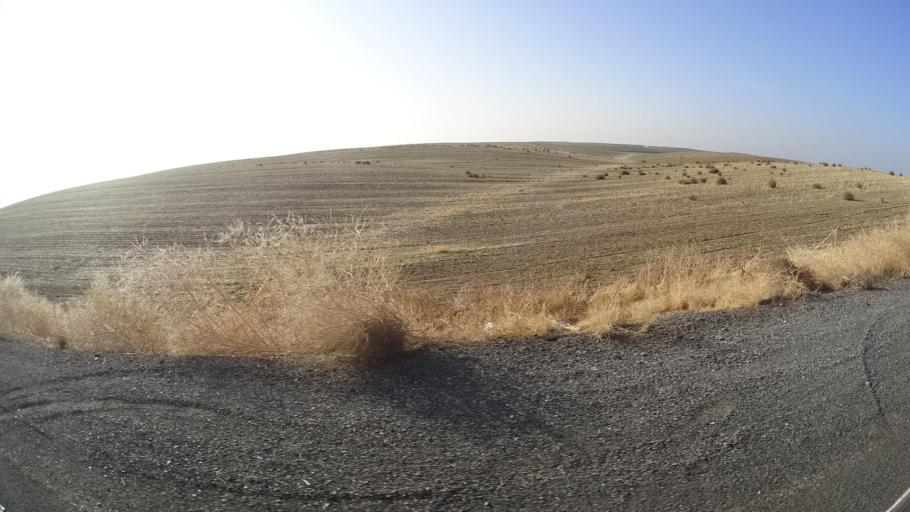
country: US
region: California
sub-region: Tulare County
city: Richgrove
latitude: 35.7619
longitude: -119.0757
